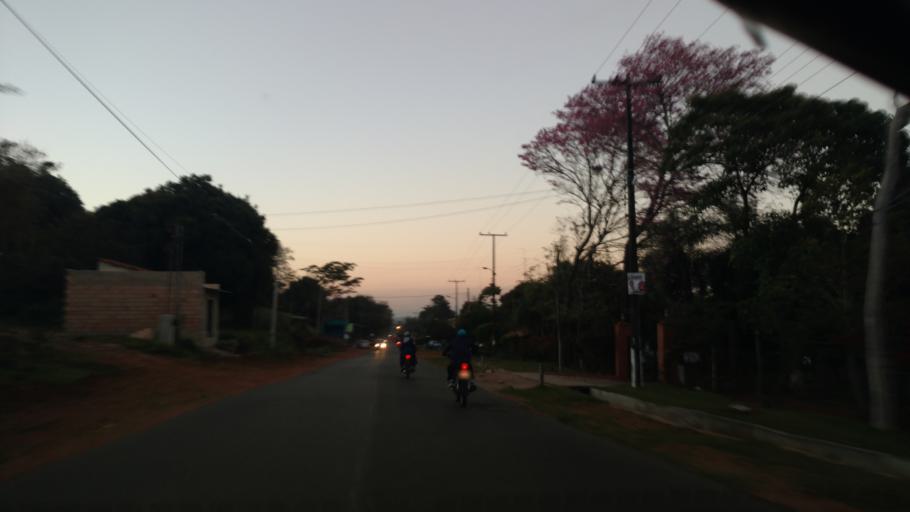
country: PY
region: Central
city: Guarambare
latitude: -25.4664
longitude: -57.4088
